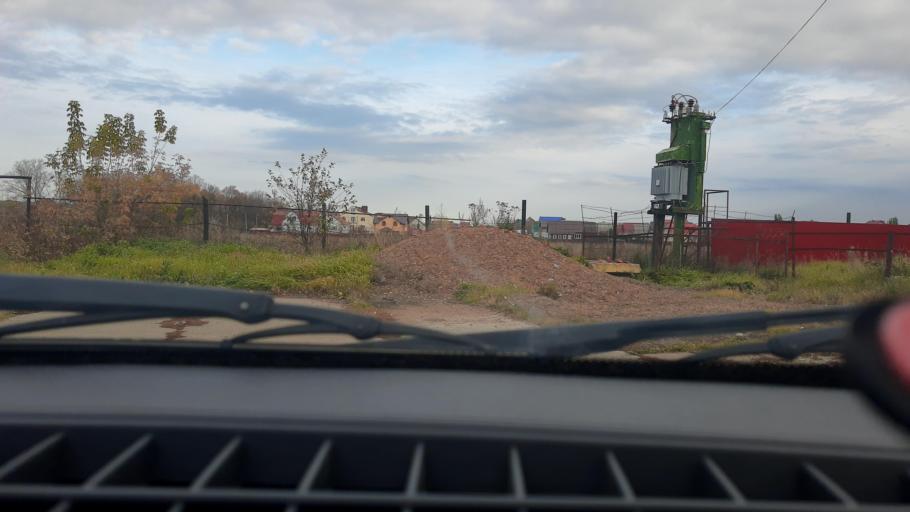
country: RU
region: Bashkortostan
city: Mikhaylovka
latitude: 54.7966
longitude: 55.9427
